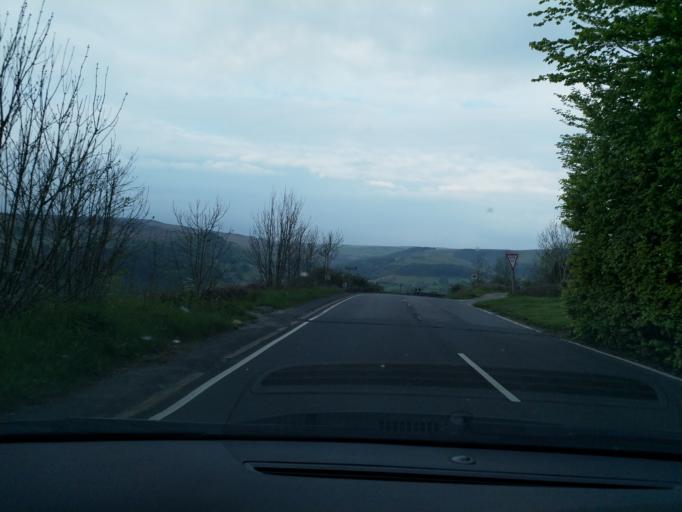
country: GB
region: England
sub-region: Derbyshire
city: Hathersage
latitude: 53.3223
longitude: -1.6370
